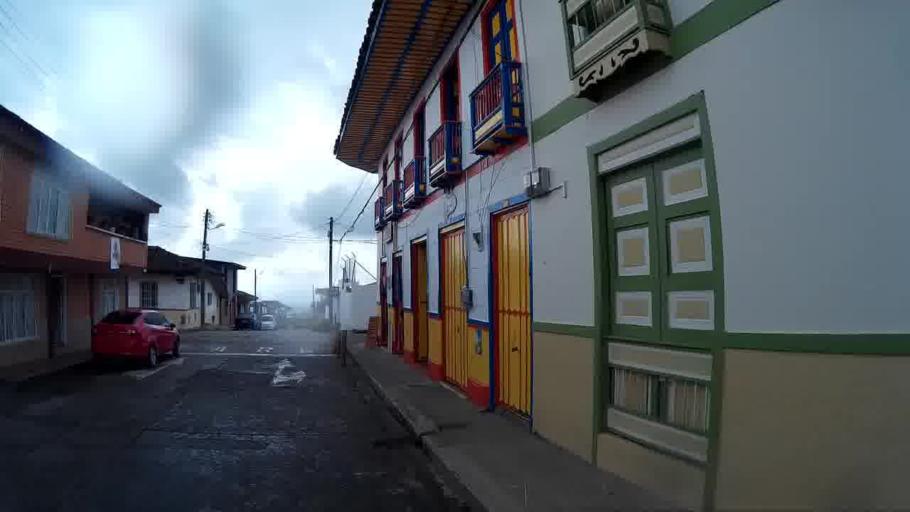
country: CO
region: Quindio
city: Filandia
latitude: 4.6765
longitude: -75.6587
